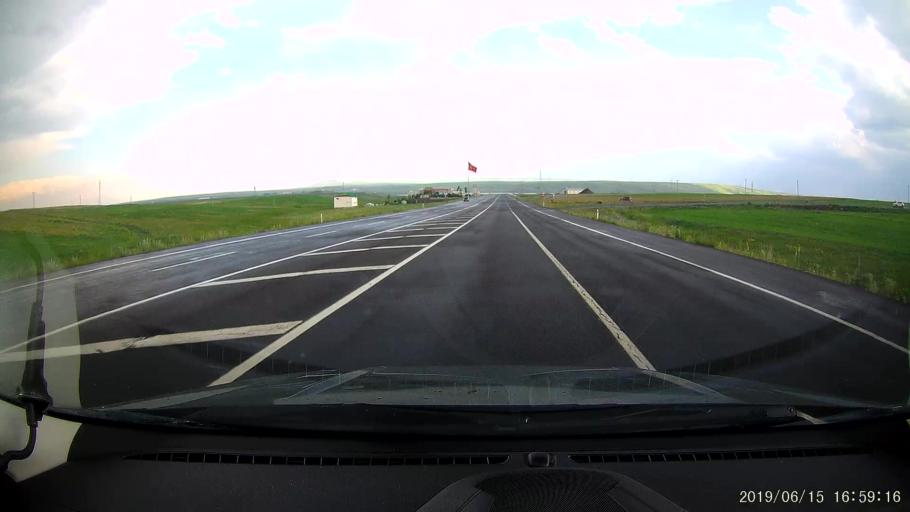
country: TR
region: Kars
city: Susuz
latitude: 40.7542
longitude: 43.1495
